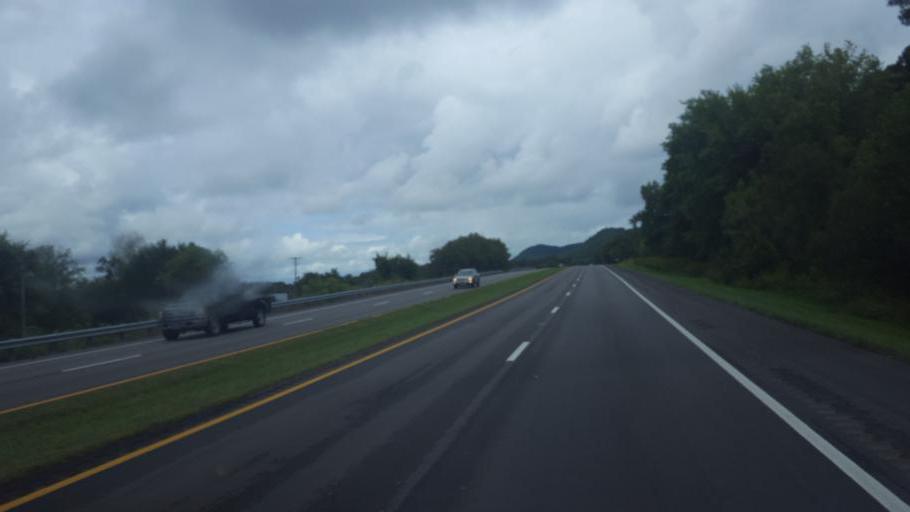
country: US
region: Ohio
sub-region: Scioto County
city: Rosemount
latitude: 38.8114
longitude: -82.9852
